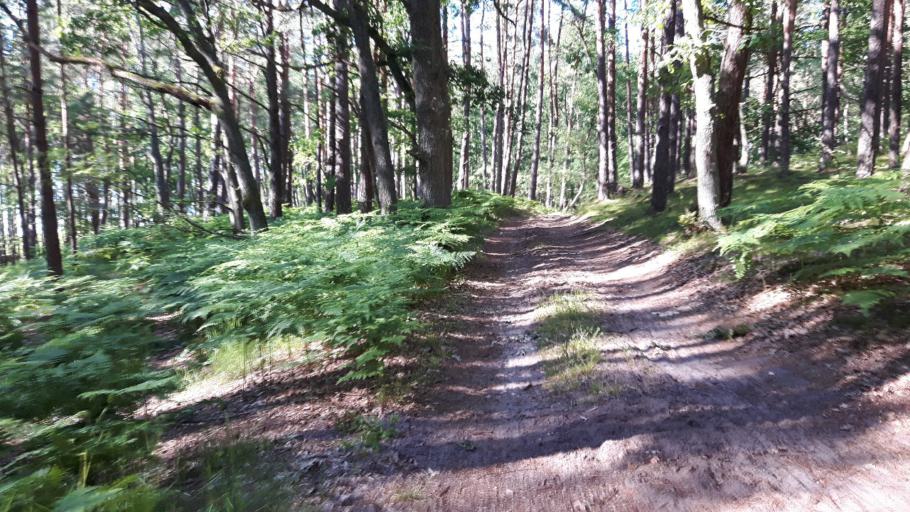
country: PL
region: Pomeranian Voivodeship
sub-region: Powiat leborski
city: Leba
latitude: 54.7136
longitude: 17.5252
